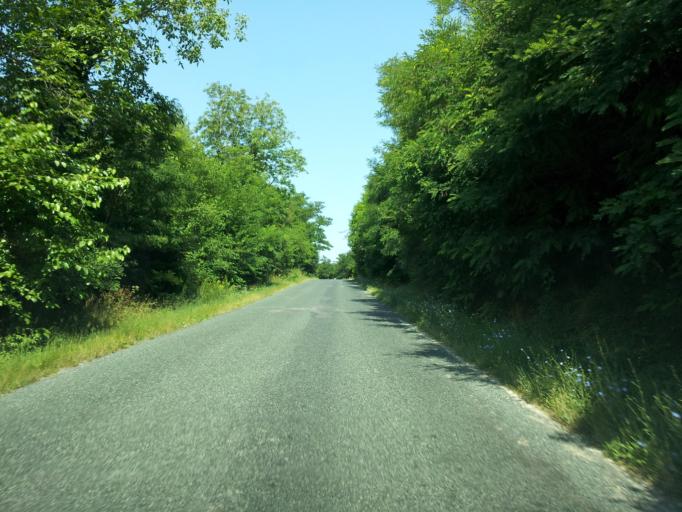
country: HU
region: Zala
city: Heviz
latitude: 46.8668
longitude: 17.1524
